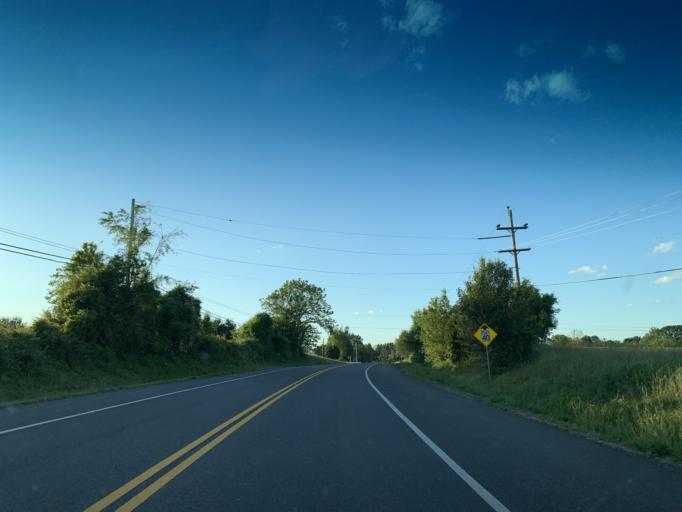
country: US
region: Maryland
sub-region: Cecil County
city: Elkton
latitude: 39.6792
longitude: -75.8604
